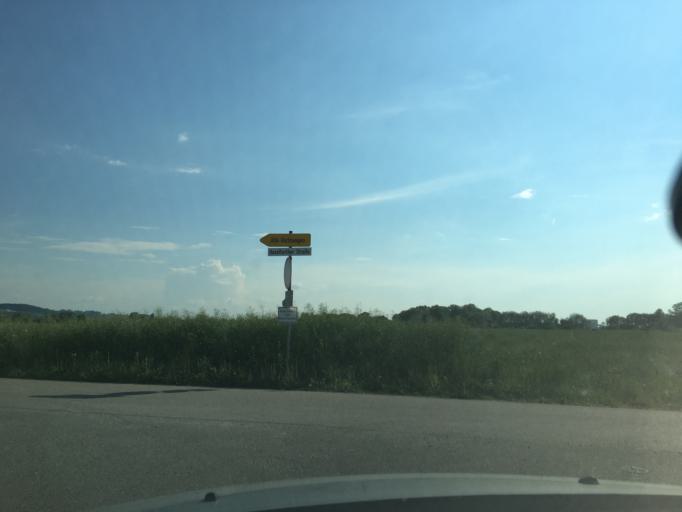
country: DE
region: Bavaria
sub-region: Lower Bavaria
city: Bruckberg
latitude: 48.4798
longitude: 12.0085
